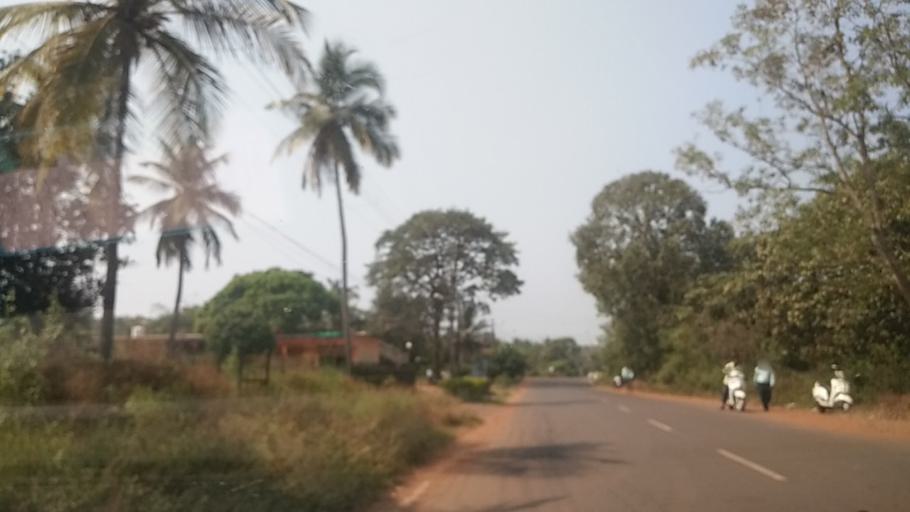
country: IN
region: Goa
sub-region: North Goa
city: Arambol
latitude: 15.6632
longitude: 73.7268
